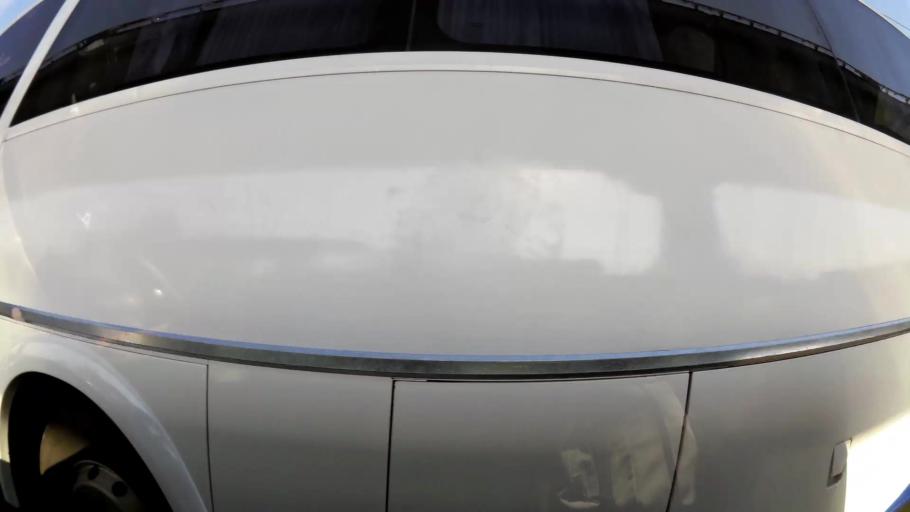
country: CL
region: Santiago Metropolitan
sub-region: Provincia de Santiago
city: La Pintana
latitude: -33.5569
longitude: -70.5862
